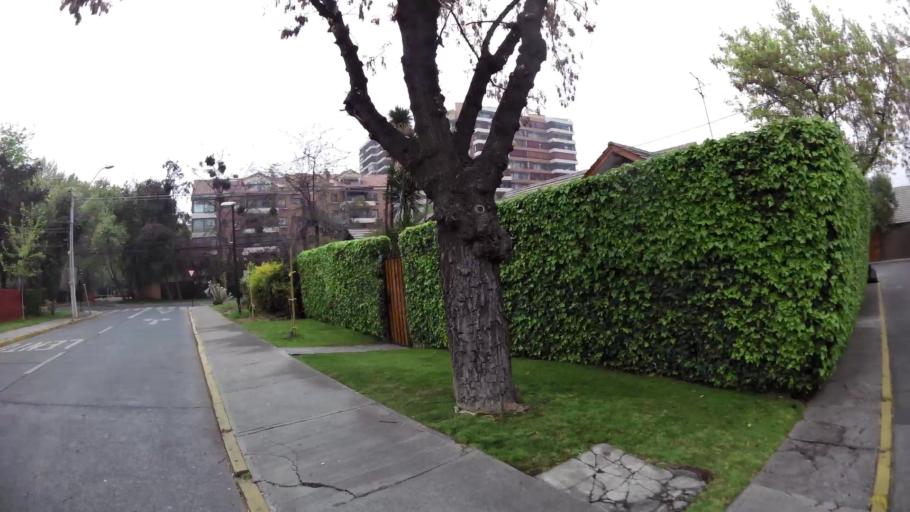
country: CL
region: Santiago Metropolitan
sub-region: Provincia de Santiago
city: Villa Presidente Frei, Nunoa, Santiago, Chile
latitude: -33.3980
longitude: -70.5798
